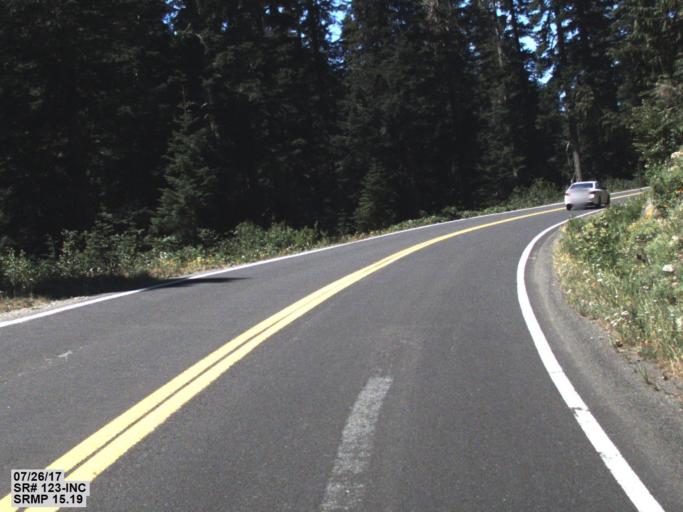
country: US
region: Washington
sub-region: King County
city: Enumclaw
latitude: 46.8563
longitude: -121.5283
